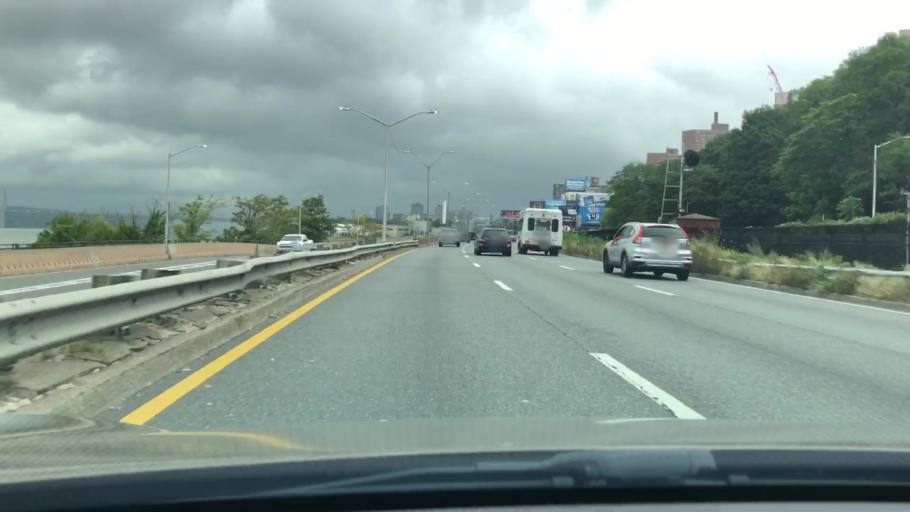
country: US
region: New Jersey
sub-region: Bergen County
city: Edgewater
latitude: 40.8160
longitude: -73.9635
